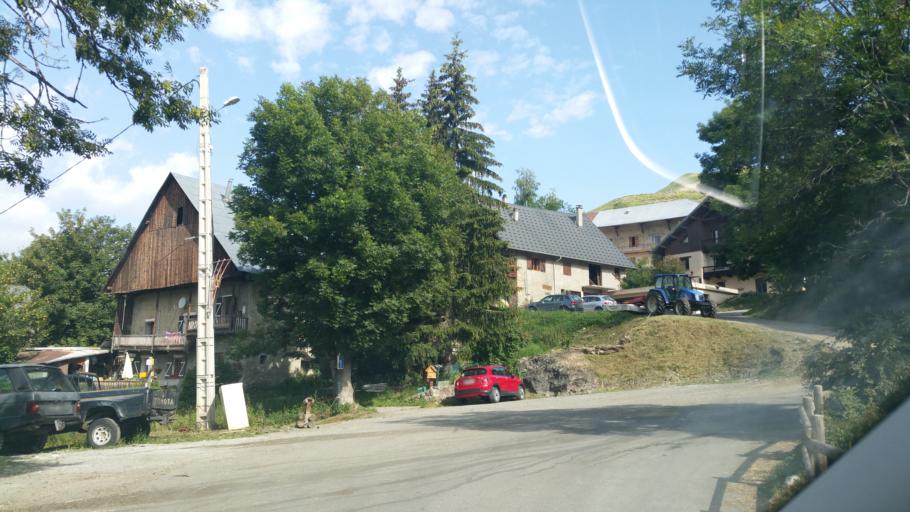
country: FR
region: Rhone-Alpes
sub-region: Departement de la Savoie
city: Saint-Jean-de-Maurienne
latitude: 45.2146
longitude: 6.2601
